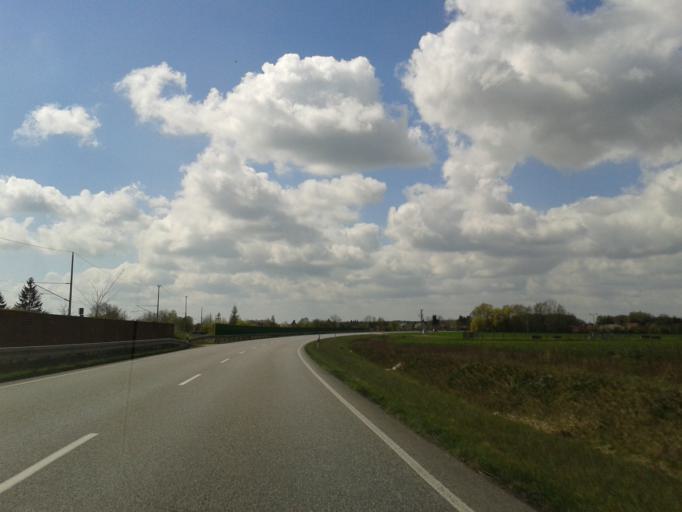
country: DE
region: Saxony-Anhalt
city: Salzwedel
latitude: 52.8589
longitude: 11.1304
